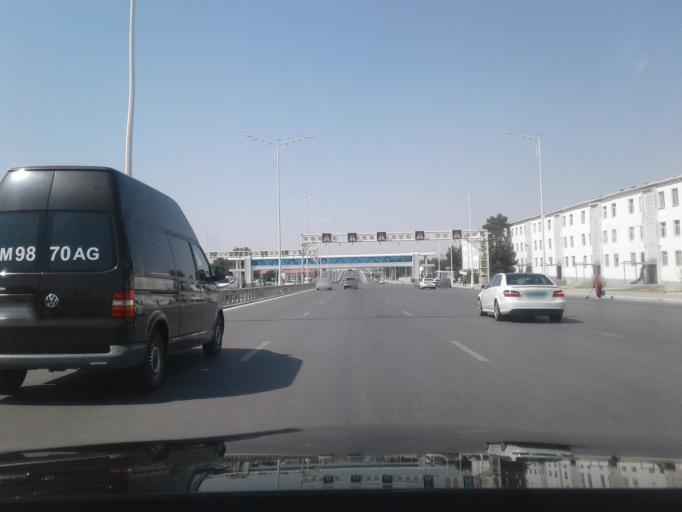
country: TM
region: Ahal
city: Ashgabat
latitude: 37.9134
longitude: 58.4236
